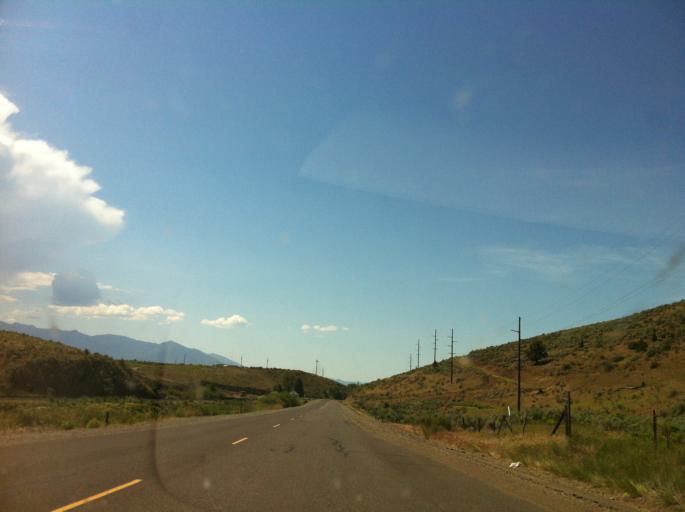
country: US
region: Oregon
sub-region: Baker County
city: Baker City
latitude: 44.7211
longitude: -117.7770
